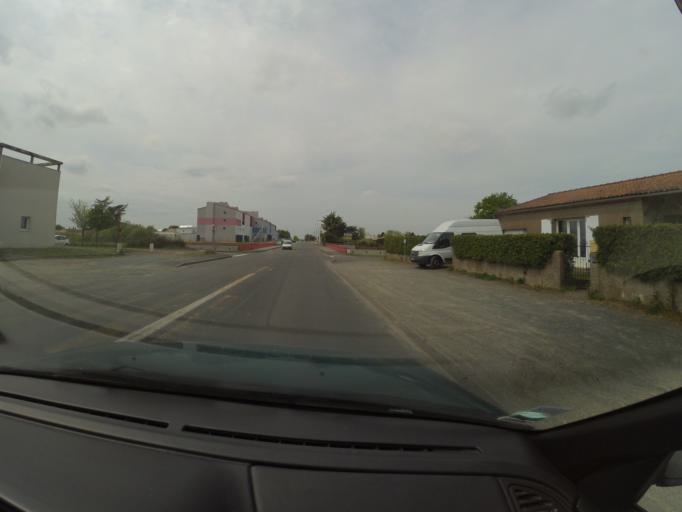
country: FR
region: Pays de la Loire
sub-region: Departement de la Loire-Atlantique
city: Gorges
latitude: 47.0954
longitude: -1.2923
